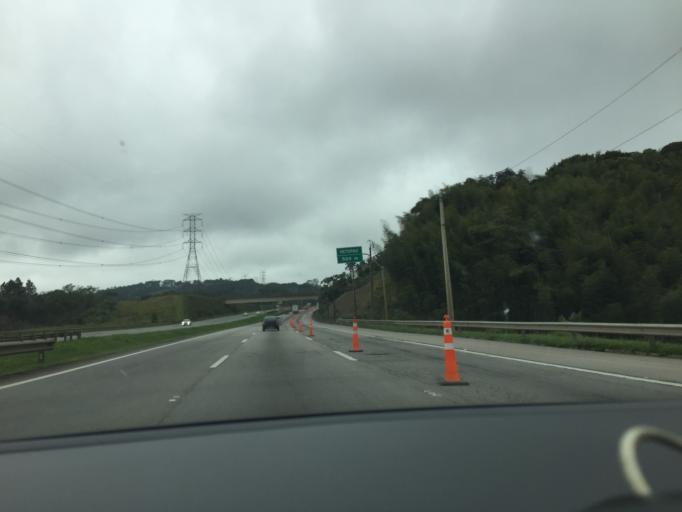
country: BR
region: Sao Paulo
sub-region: Embu-Guacu
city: Embu Guacu
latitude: -23.8041
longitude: -46.7051
